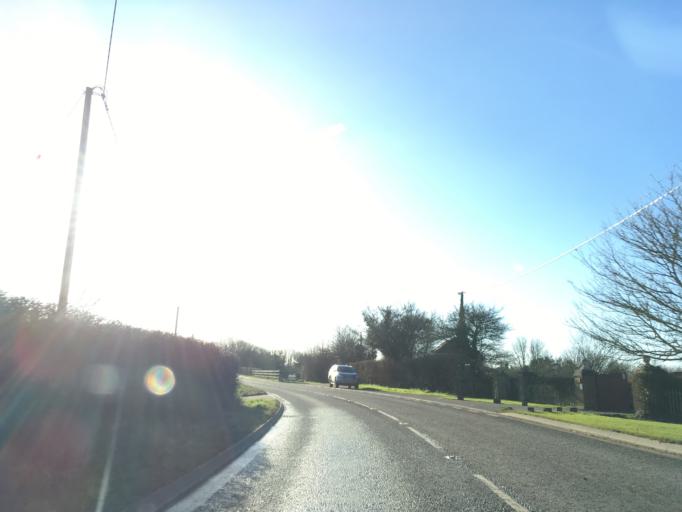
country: GB
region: England
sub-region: Wiltshire
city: Minety
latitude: 51.6164
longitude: -1.9499
